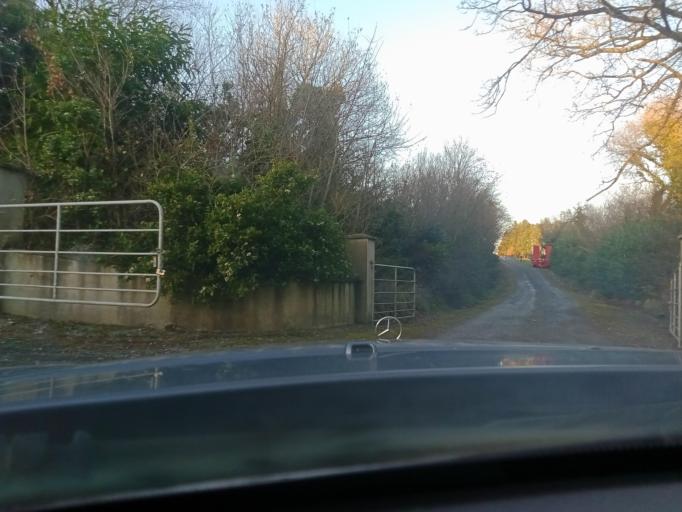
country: IE
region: Leinster
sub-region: Kilkenny
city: Graiguenamanagh
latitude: 52.4857
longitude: -6.9544
